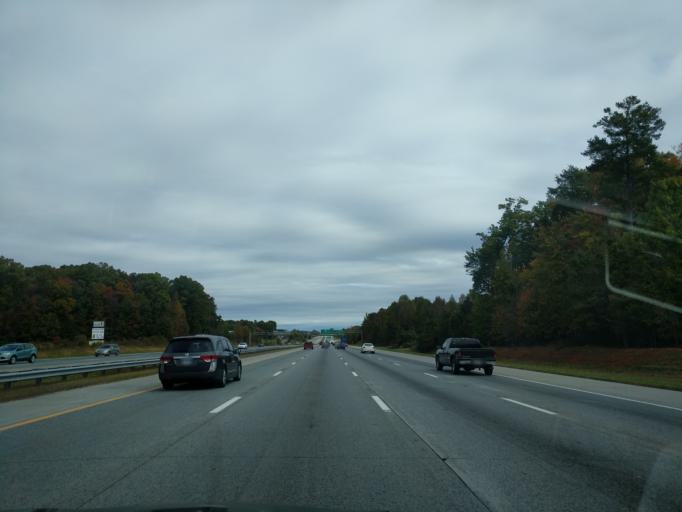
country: US
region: North Carolina
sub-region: Rowan County
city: Salisbury
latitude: 35.6243
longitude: -80.5020
